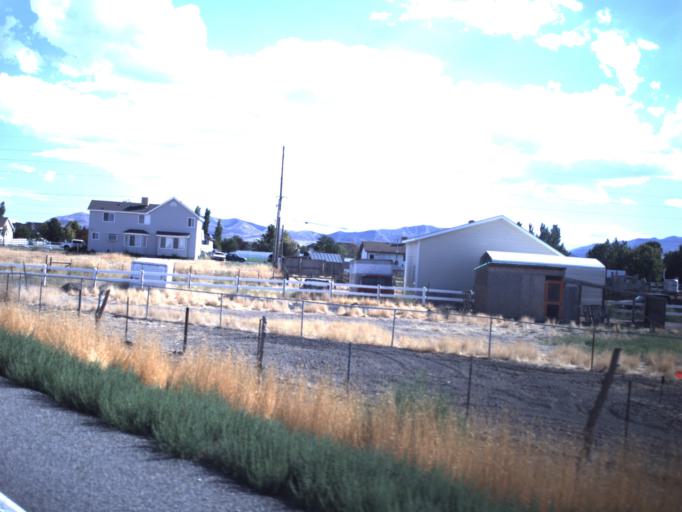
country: US
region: Utah
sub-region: Tooele County
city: Grantsville
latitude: 40.5936
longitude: -112.4249
